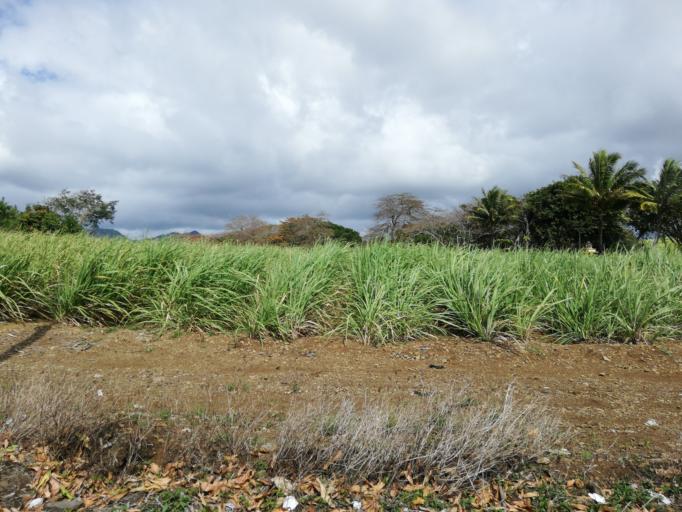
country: MU
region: Flacq
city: Camp Ithier
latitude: -20.2084
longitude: 57.7294
